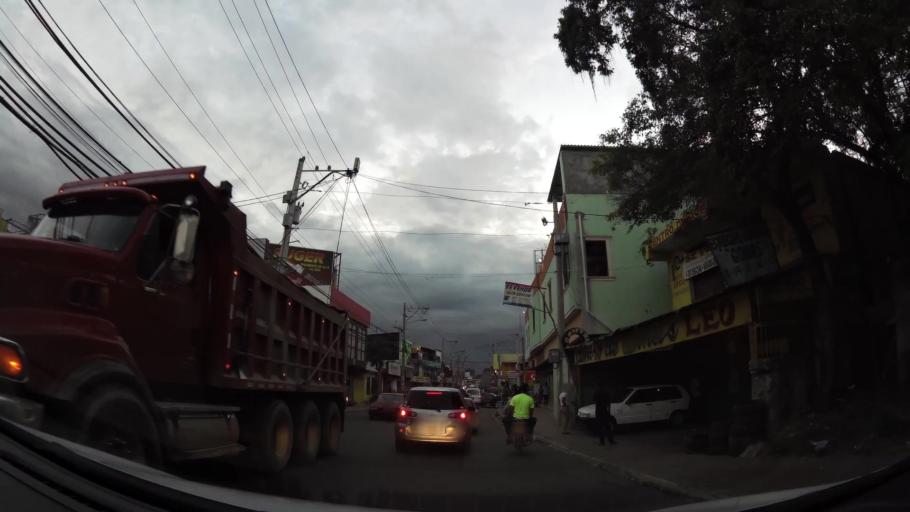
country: DO
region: Santo Domingo
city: Santo Domingo Oeste
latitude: 18.5240
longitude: -70.0318
